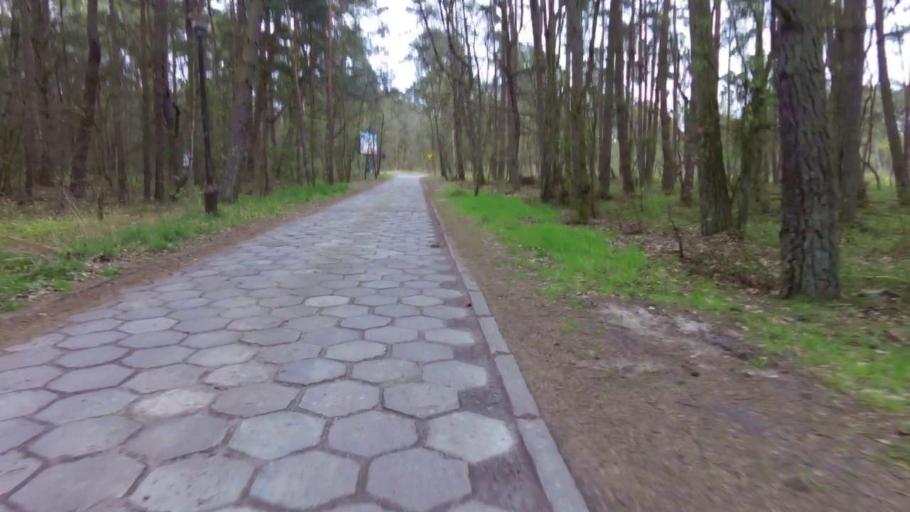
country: PL
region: West Pomeranian Voivodeship
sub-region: Powiat kamienski
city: Dziwnow
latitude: 53.9999
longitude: 14.6733
